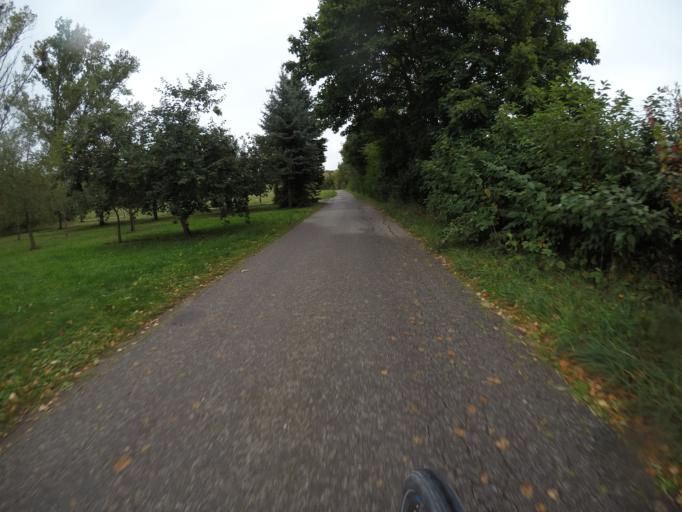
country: DE
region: Baden-Wuerttemberg
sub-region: Regierungsbezirk Stuttgart
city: Leonberg
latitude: 48.7794
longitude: 9.0288
